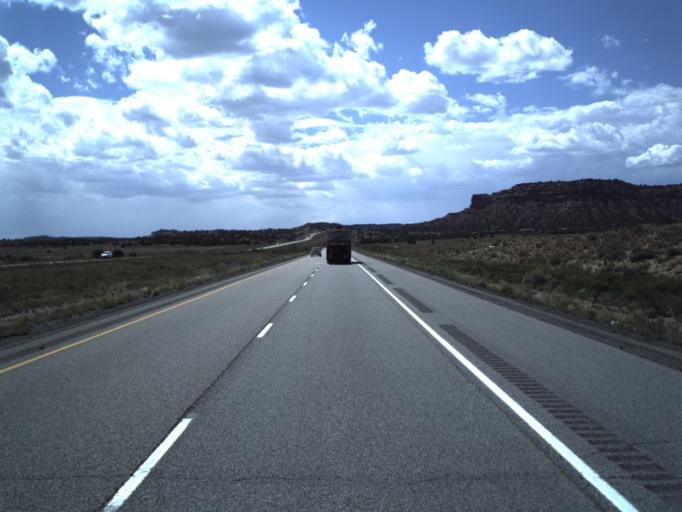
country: US
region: Utah
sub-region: Emery County
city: Castle Dale
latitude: 38.8724
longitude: -110.6854
